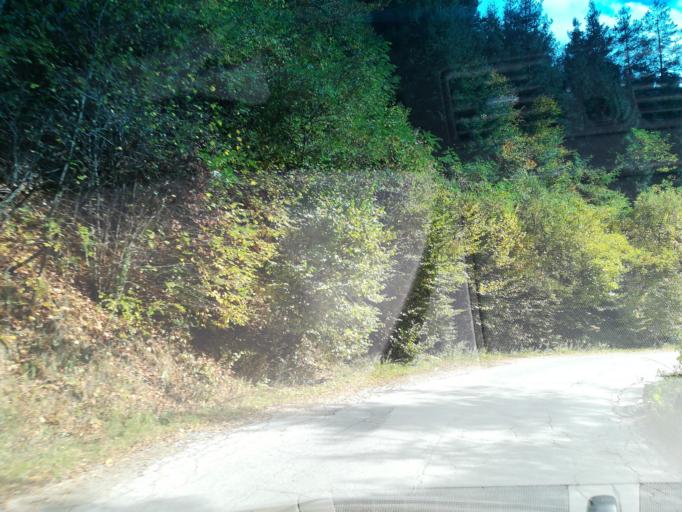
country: BG
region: Pazardzhik
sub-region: Obshtina Batak
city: Batak
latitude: 41.9472
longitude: 24.2475
